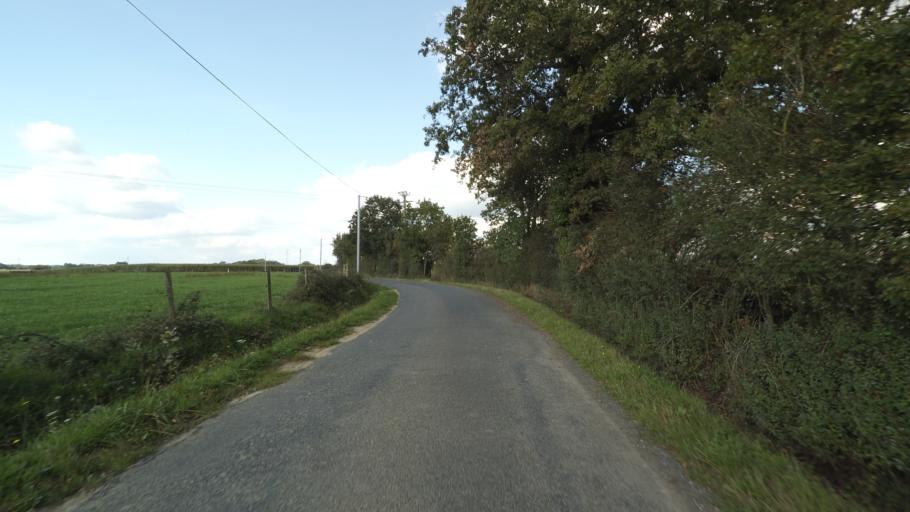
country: FR
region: Pays de la Loire
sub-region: Departement de la Loire-Atlantique
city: Vieillevigne
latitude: 46.9783
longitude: -1.4088
